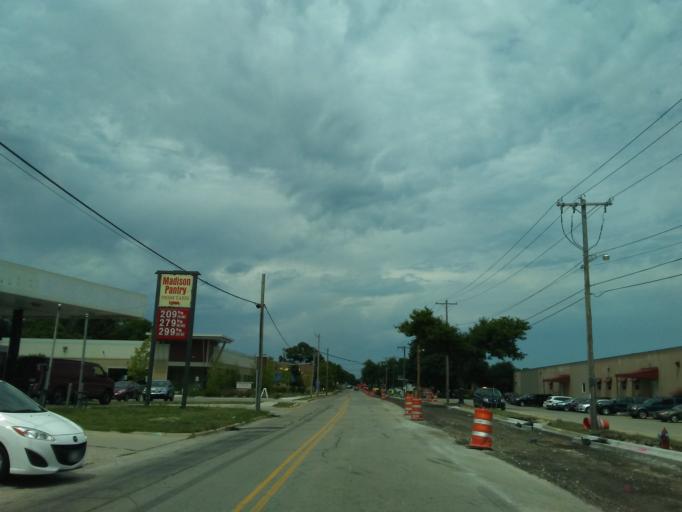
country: US
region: Wisconsin
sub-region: Dane County
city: Maple Bluff
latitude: 43.0985
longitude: -89.3641
